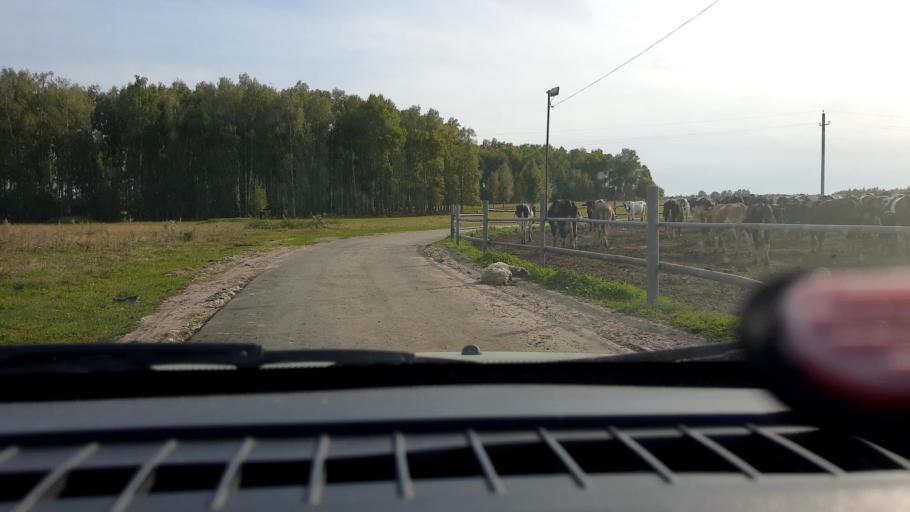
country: RU
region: Nizjnij Novgorod
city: Kstovo
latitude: 55.9955
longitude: 44.2216
